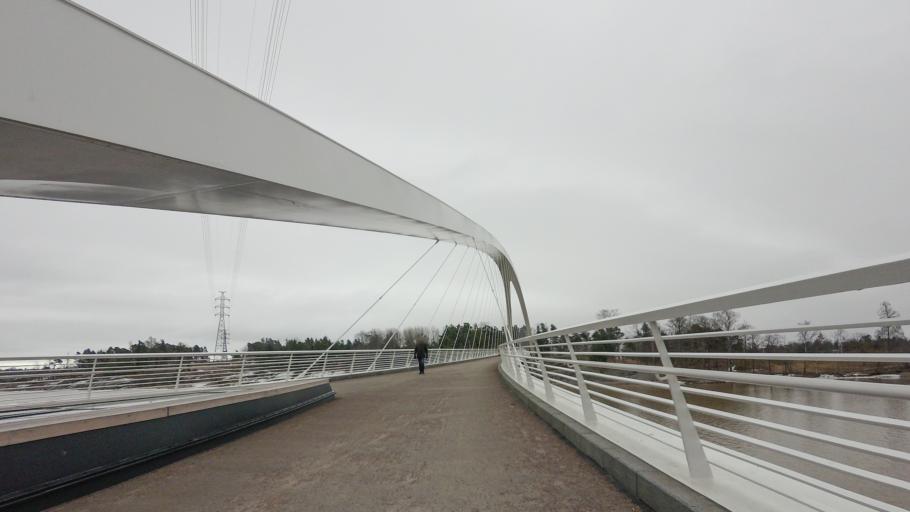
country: FI
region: Uusimaa
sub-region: Helsinki
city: Helsinki
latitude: 60.1824
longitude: 24.9820
